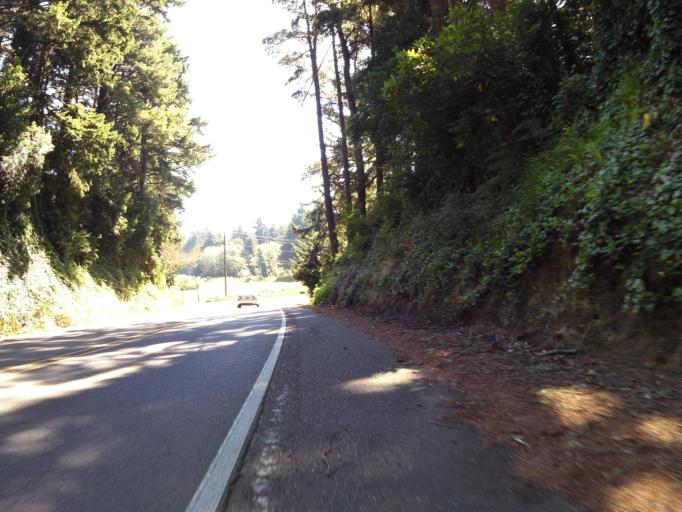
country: US
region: Oregon
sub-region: Coos County
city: Barview
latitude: 43.3457
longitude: -124.3150
